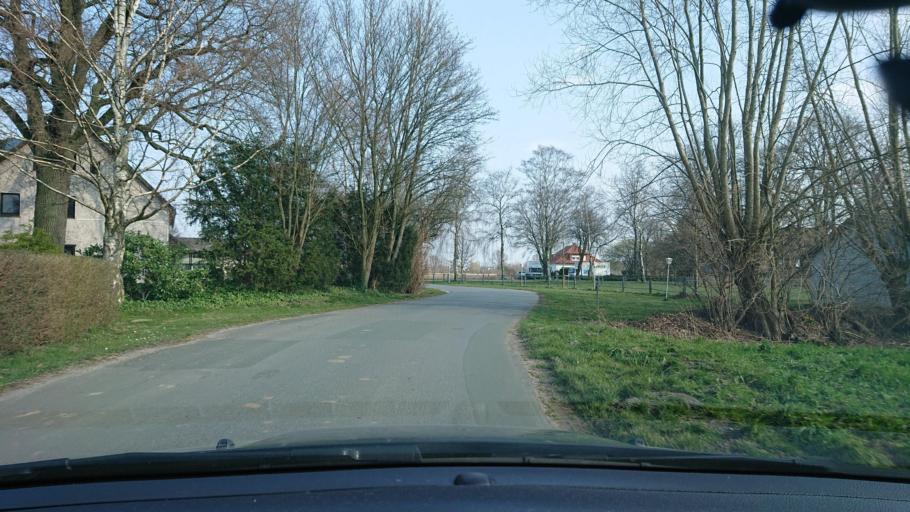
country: DE
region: North Rhine-Westphalia
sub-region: Regierungsbezirk Detmold
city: Langenberg
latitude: 51.7714
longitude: 8.3699
